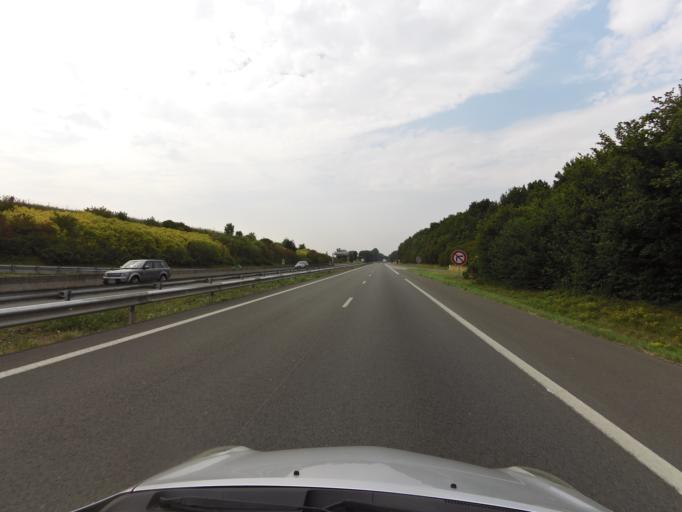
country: FR
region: Nord-Pas-de-Calais
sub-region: Departement du Pas-de-Calais
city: Bourlon
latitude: 50.1450
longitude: 3.1259
